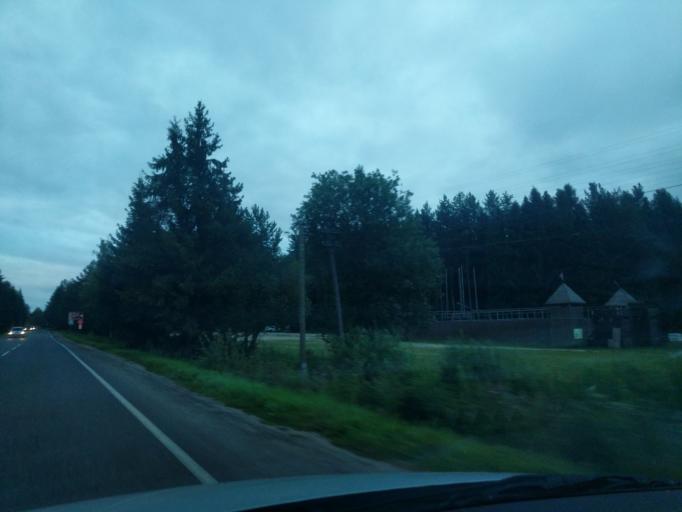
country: RU
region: Kirov
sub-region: Kirovo-Chepetskiy Rayon
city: Kirov
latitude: 58.6060
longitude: 49.8109
